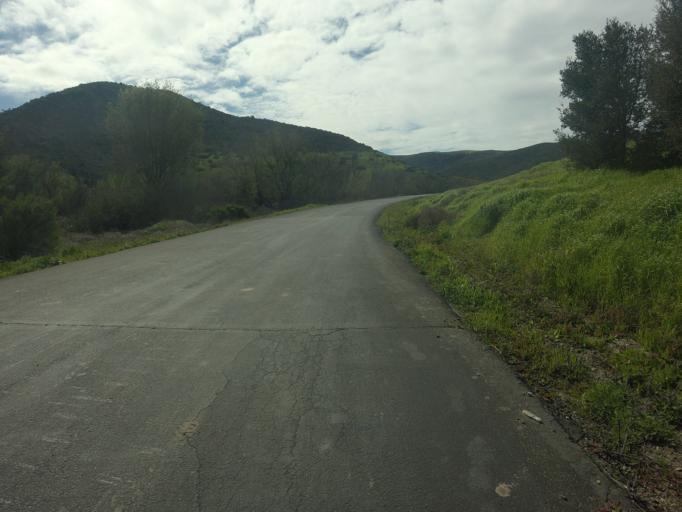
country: US
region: California
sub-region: Orange County
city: Aliso Viejo
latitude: 33.5438
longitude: -117.7288
